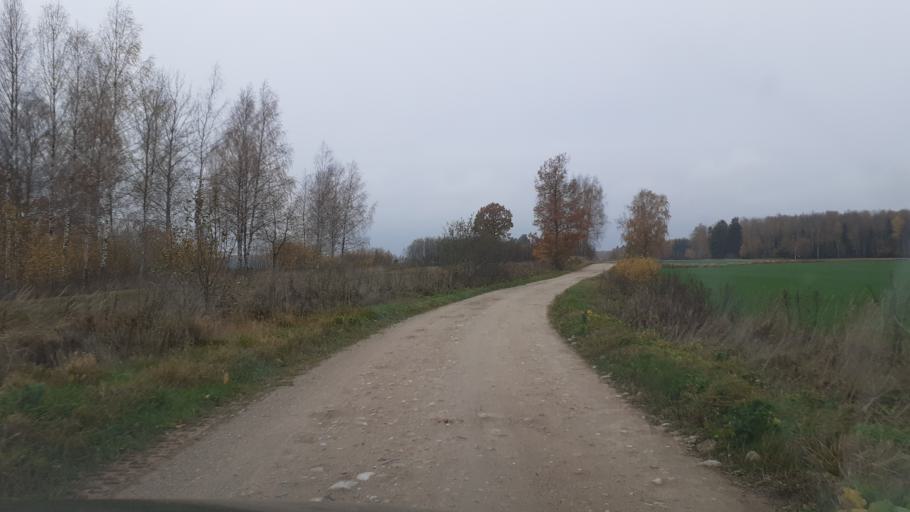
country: LV
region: Saldus Rajons
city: Saldus
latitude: 56.8702
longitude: 22.3340
